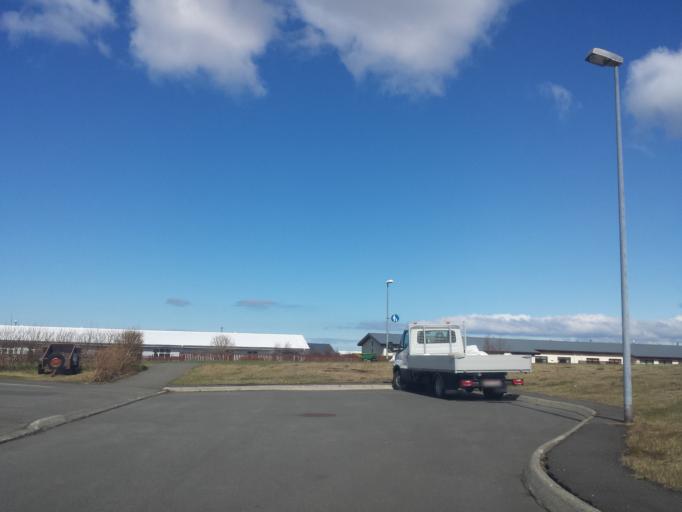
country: IS
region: Capital Region
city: Reykjavik
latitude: 64.0965
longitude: -21.8575
